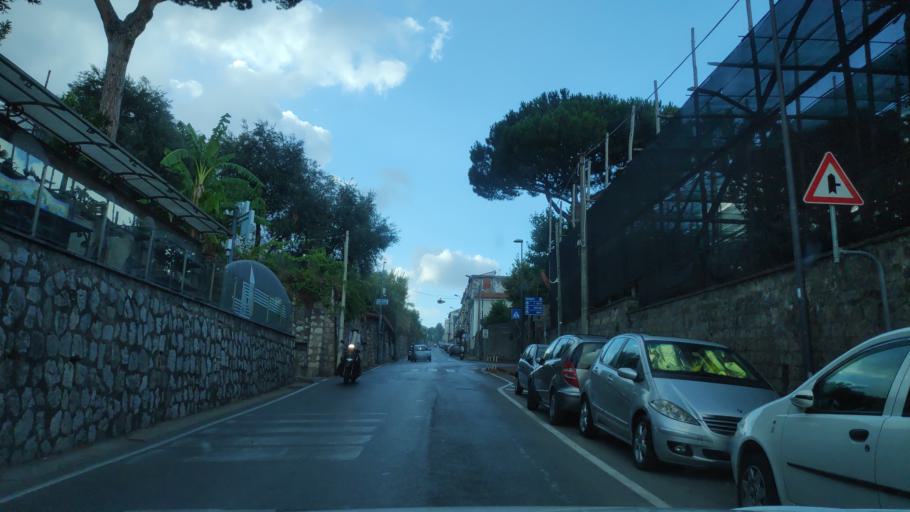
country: IT
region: Campania
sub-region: Provincia di Napoli
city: Piano di Sorrento
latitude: 40.6339
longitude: 14.4176
